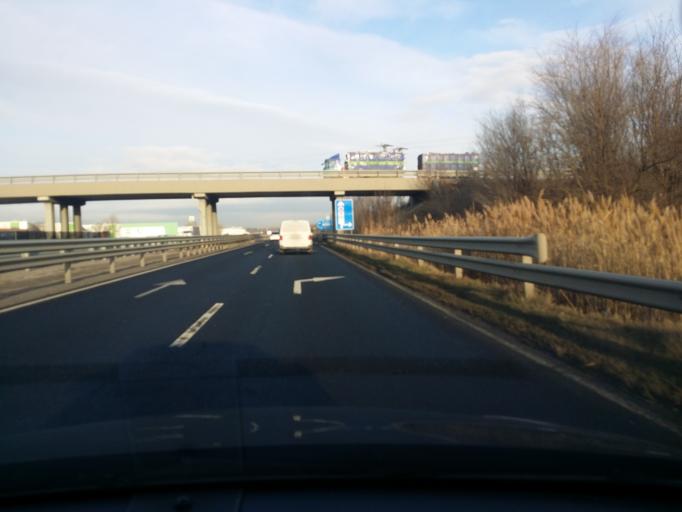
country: HU
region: Pest
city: Gyal
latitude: 47.3564
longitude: 19.1999
